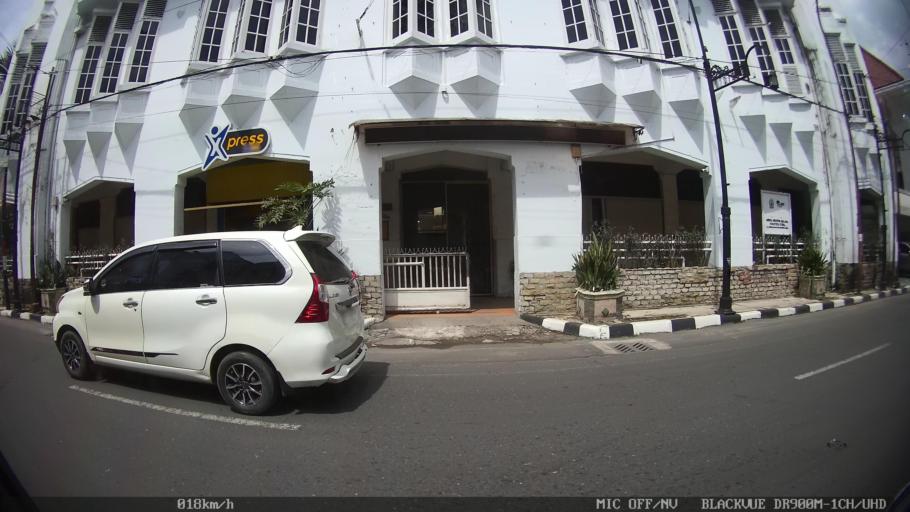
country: ID
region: North Sumatra
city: Medan
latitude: 3.5850
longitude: 98.6804
